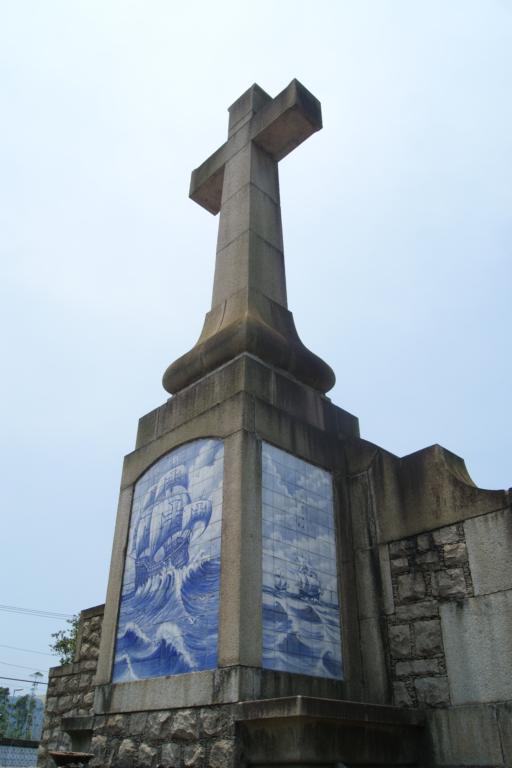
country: BR
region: Sao Paulo
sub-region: Cubatao
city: Cubatao
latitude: -23.8730
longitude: -46.4284
